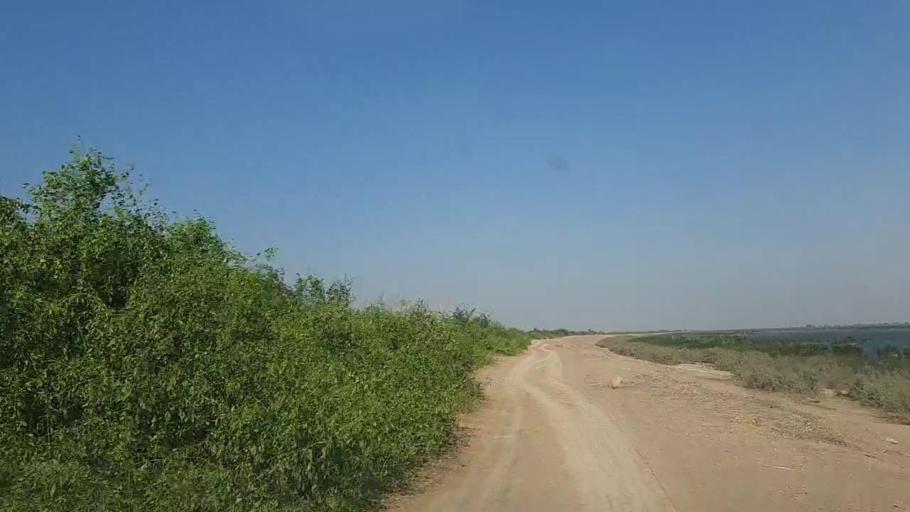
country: PK
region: Sindh
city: Daro Mehar
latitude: 24.9213
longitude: 68.0784
